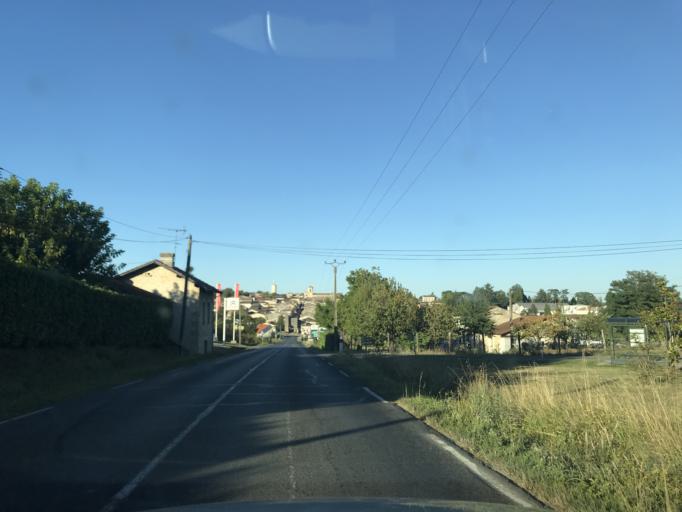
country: FR
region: Aquitaine
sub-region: Departement de la Gironde
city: Sauveterre-de-Guyenne
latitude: 44.6883
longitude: -0.0908
